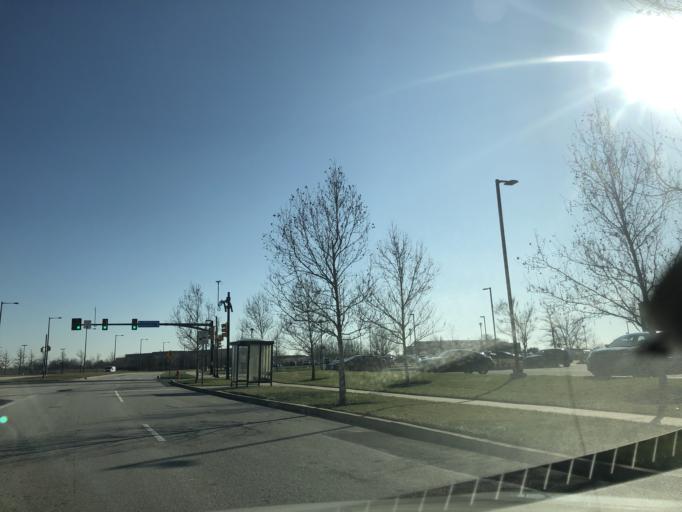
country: US
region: New Jersey
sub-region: Gloucester County
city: National Park
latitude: 39.8967
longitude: -75.1716
